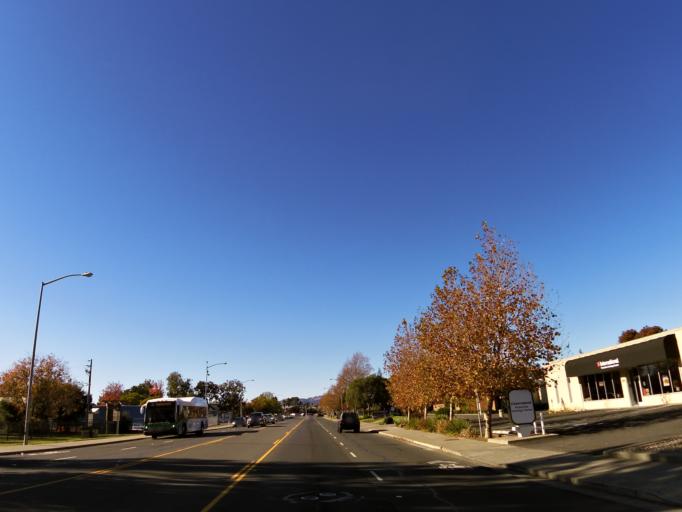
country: US
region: California
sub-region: Solano County
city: Fairfield
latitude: 38.2493
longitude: -122.0617
